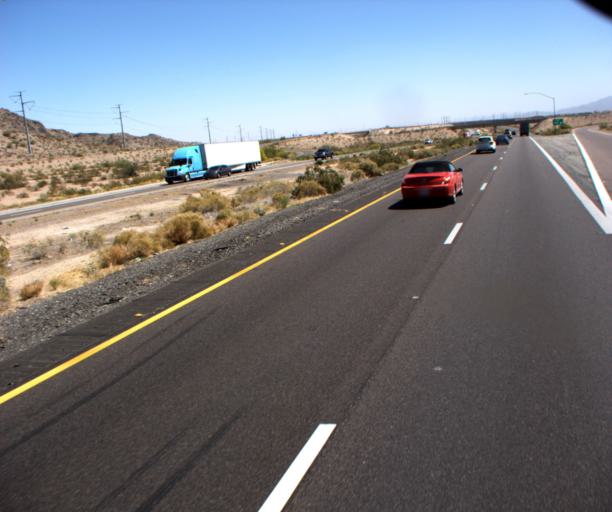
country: US
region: Arizona
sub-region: Maricopa County
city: Buckeye
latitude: 33.4288
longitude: -112.6319
